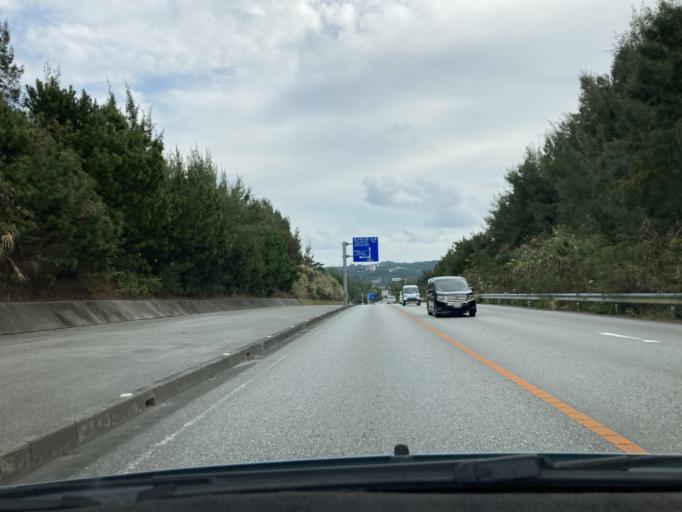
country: JP
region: Okinawa
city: Ishikawa
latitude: 26.5043
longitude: 127.8759
